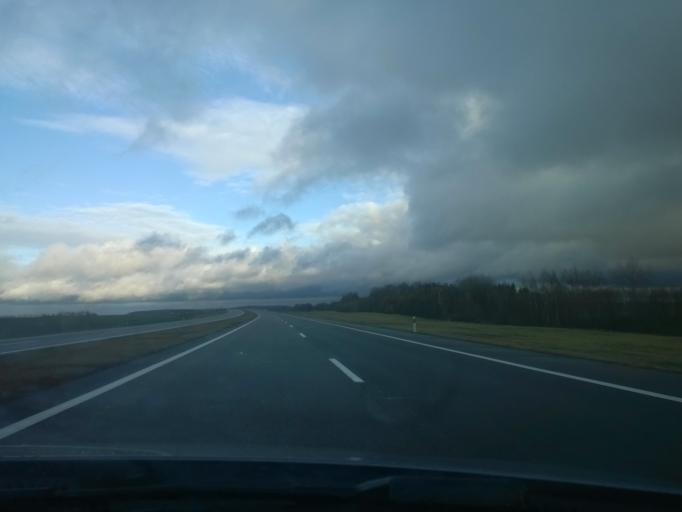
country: BY
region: Brest
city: Baranovichi
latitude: 53.2139
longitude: 26.1331
